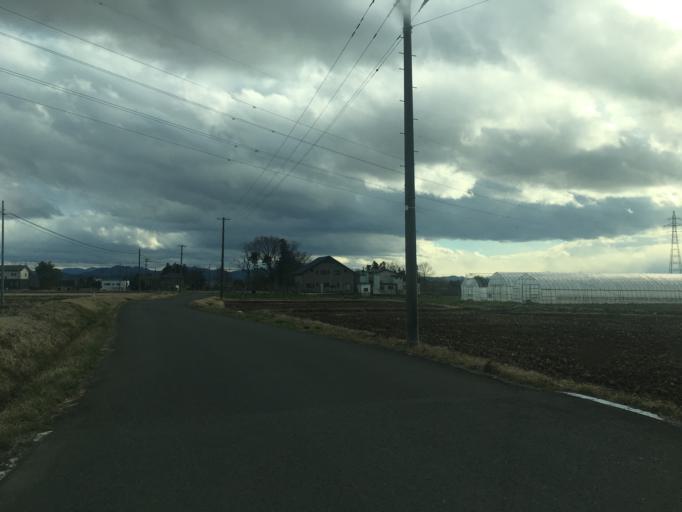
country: JP
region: Fukushima
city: Yanagawamachi-saiwaicho
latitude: 37.8778
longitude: 140.5738
